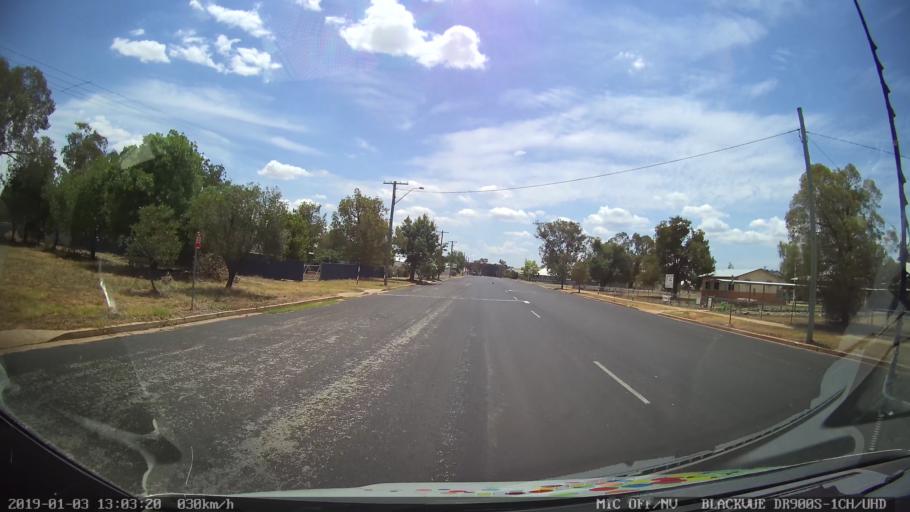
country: AU
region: New South Wales
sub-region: Cabonne
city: Canowindra
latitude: -33.6173
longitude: 148.4352
